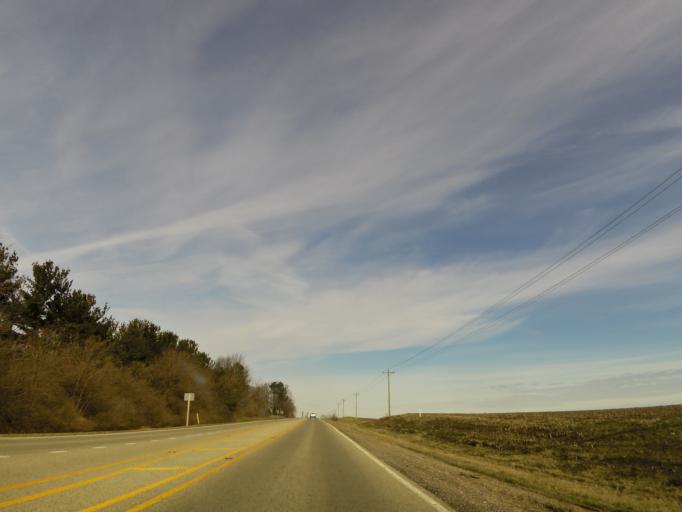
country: US
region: Illinois
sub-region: McLean County
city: Normal
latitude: 40.5101
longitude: -89.0349
